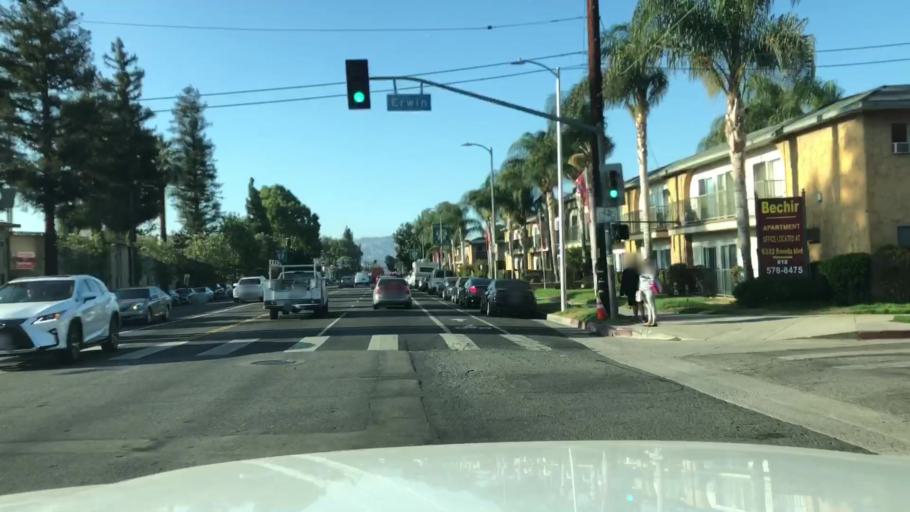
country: US
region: California
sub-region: Los Angeles County
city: Northridge
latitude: 34.1839
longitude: -118.5360
